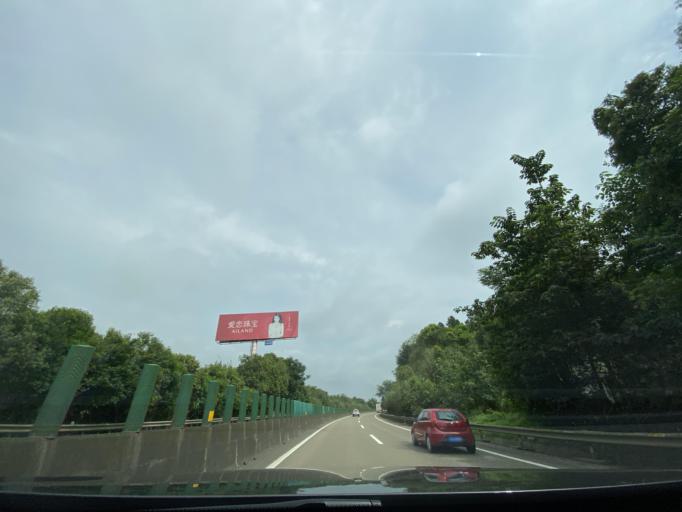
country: CN
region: Sichuan
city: Chonglong
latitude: 29.7204
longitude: 104.9359
